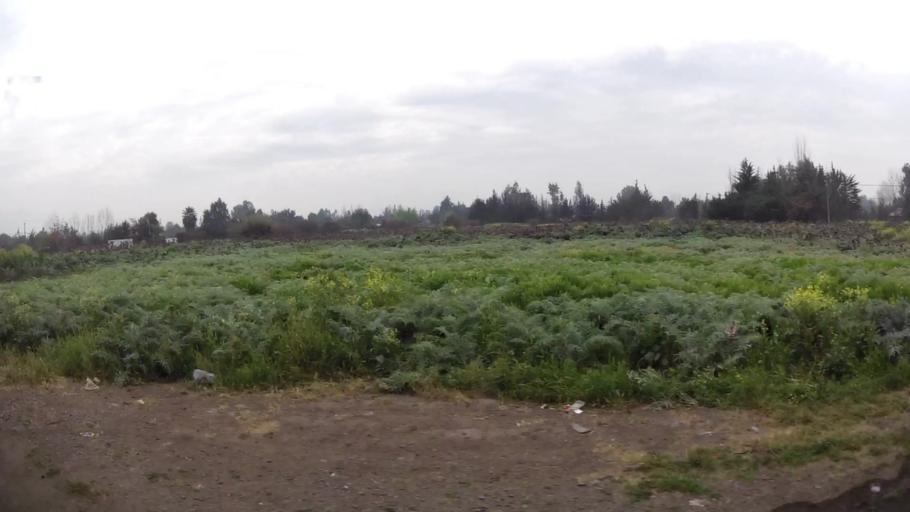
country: CL
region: Santiago Metropolitan
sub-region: Provincia de Chacabuco
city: Lampa
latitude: -33.2431
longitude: -70.7742
